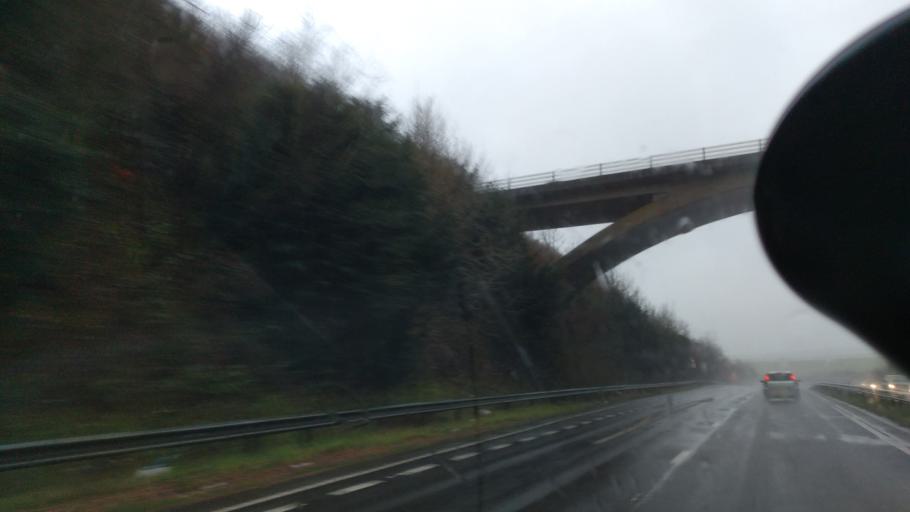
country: GB
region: England
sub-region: Brighton and Hove
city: Brighton
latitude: 50.8688
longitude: -0.1178
